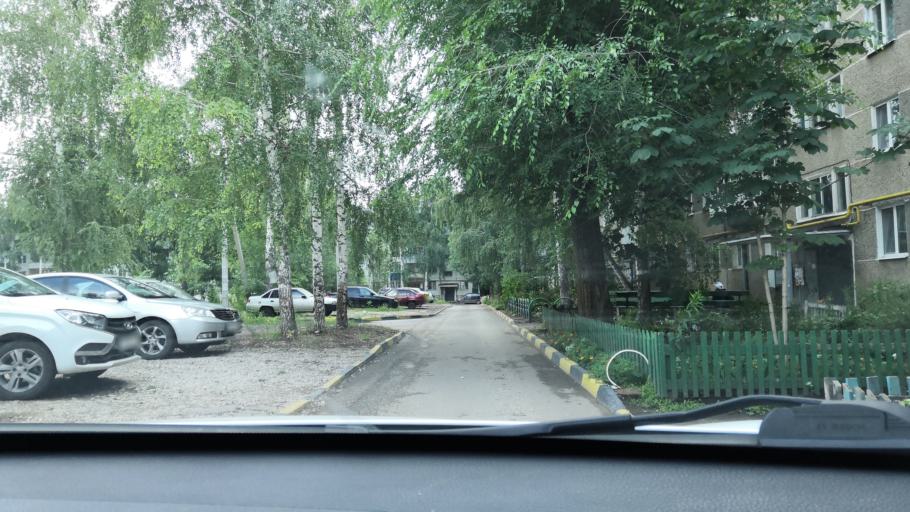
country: RU
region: Samara
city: Smyshlyayevka
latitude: 53.2701
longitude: 50.3871
